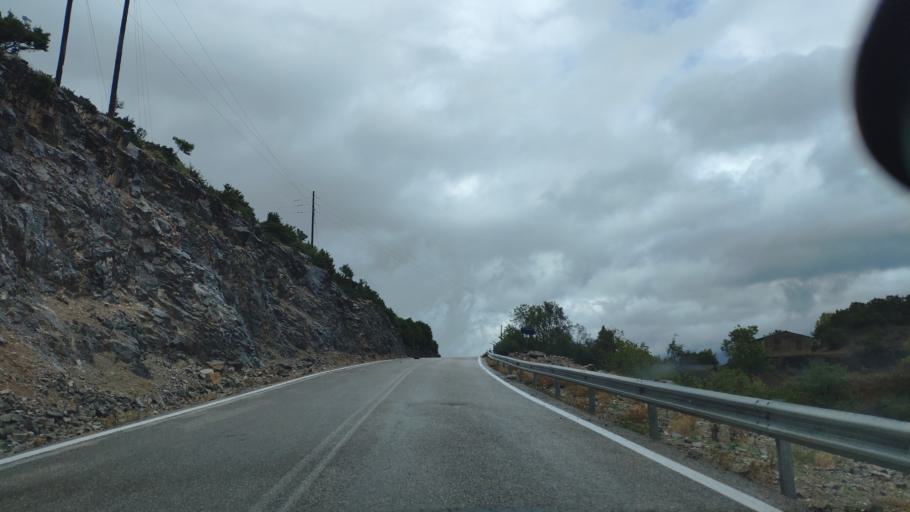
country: GR
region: Thessaly
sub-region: Nomos Kardhitsas
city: Anthiro
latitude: 39.1038
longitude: 21.4093
